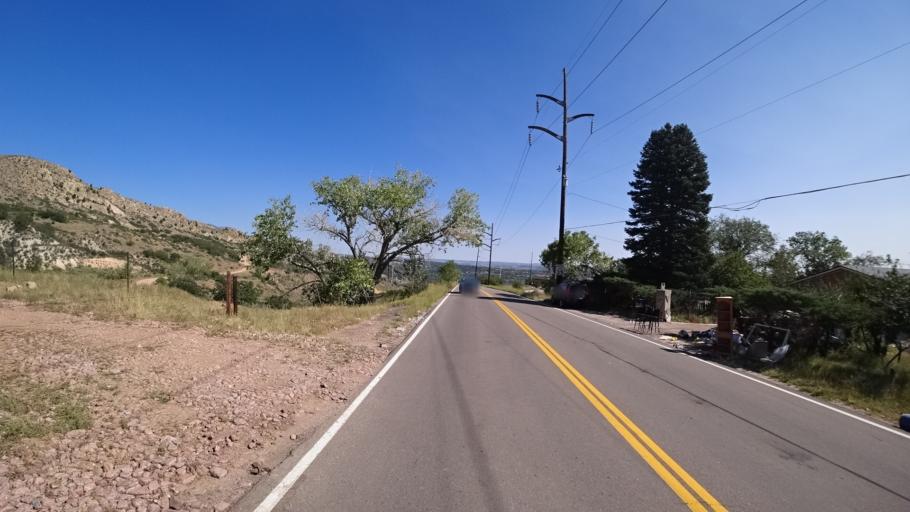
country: US
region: Colorado
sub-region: El Paso County
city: Manitou Springs
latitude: 38.8318
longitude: -104.8786
